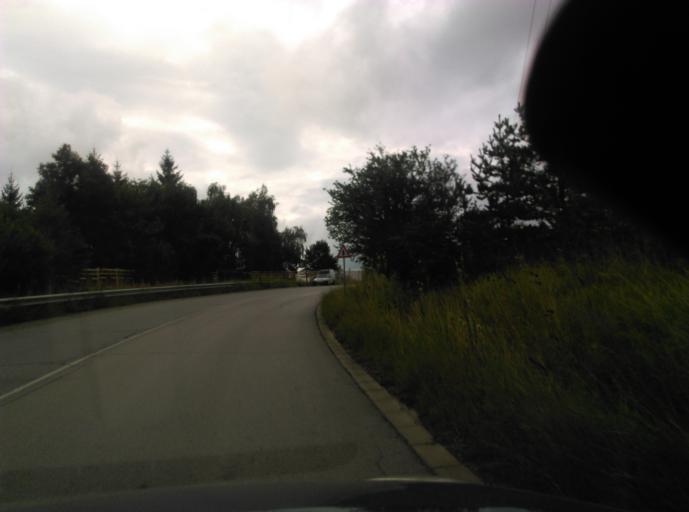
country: BG
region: Sofia-Capital
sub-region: Stolichna Obshtina
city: Sofia
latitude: 42.5960
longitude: 23.3590
